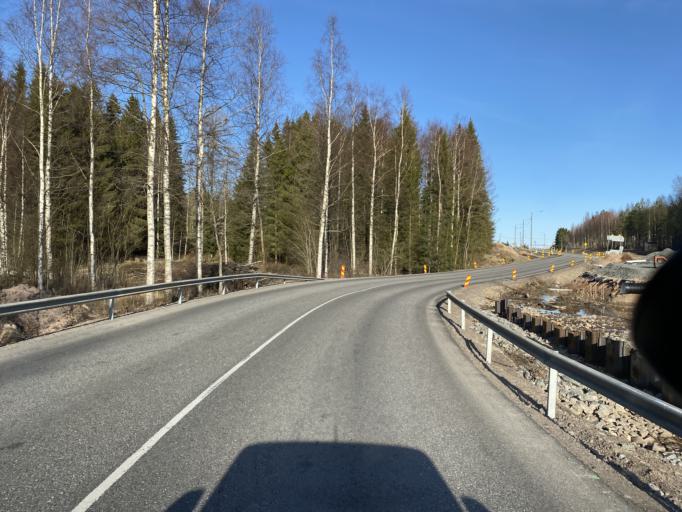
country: FI
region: Satakunta
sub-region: Rauma
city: Koeylioe
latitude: 61.1627
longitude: 22.3094
